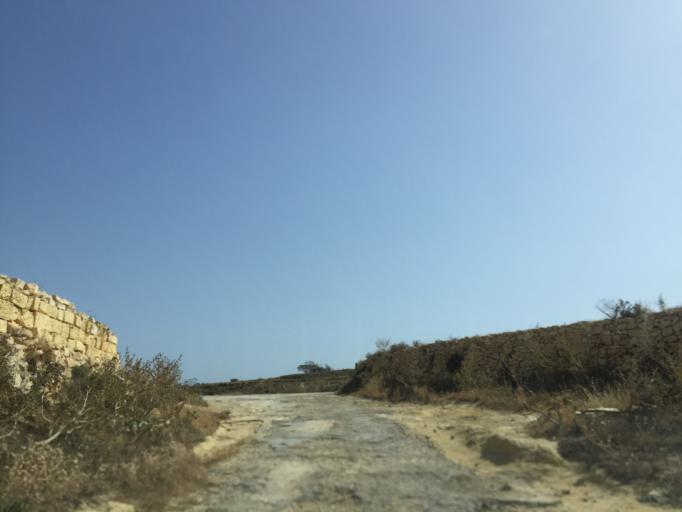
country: MT
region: L-Gharb
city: Gharb
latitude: 36.0718
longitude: 14.2035
